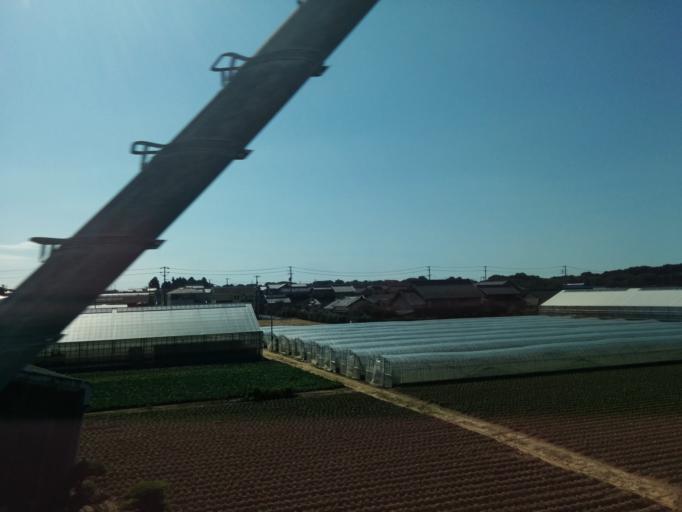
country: JP
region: Shizuoka
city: Kosai-shi
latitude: 34.7173
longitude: 137.4735
